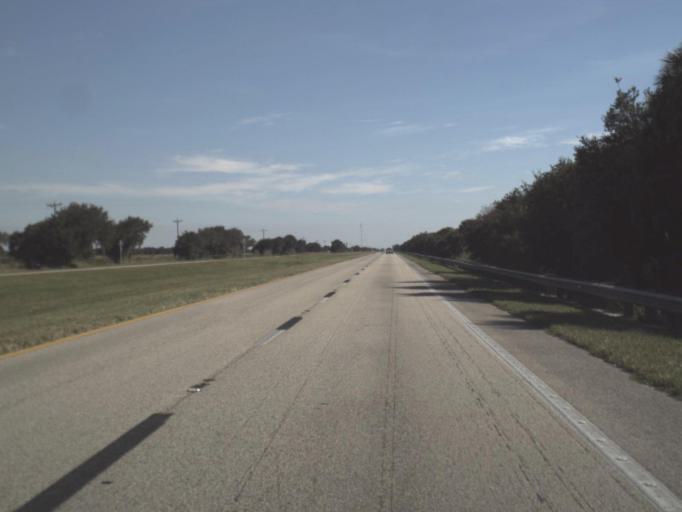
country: US
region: Florida
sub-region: Glades County
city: Moore Haven
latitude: 26.8918
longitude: -81.2364
